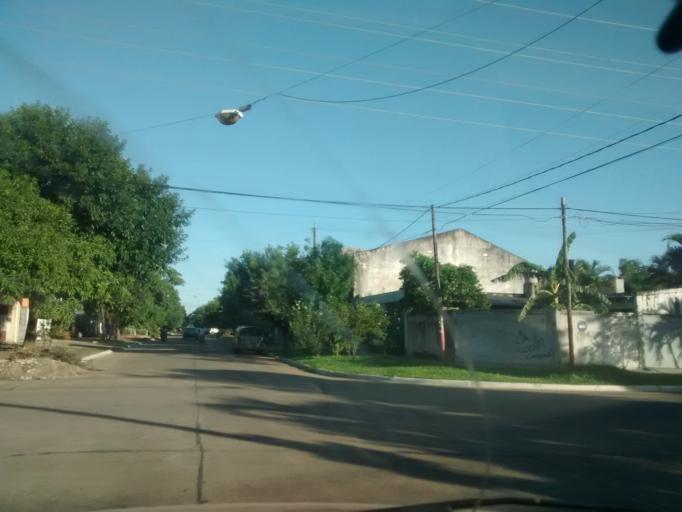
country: AR
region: Chaco
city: Resistencia
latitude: -27.4622
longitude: -58.9937
